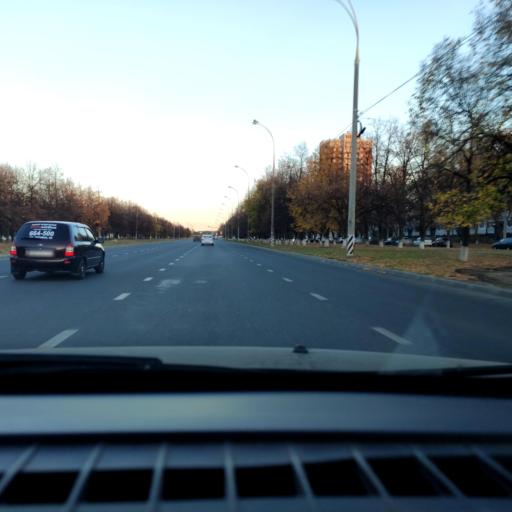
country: RU
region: Samara
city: Tol'yatti
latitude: 53.5191
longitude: 49.2860
